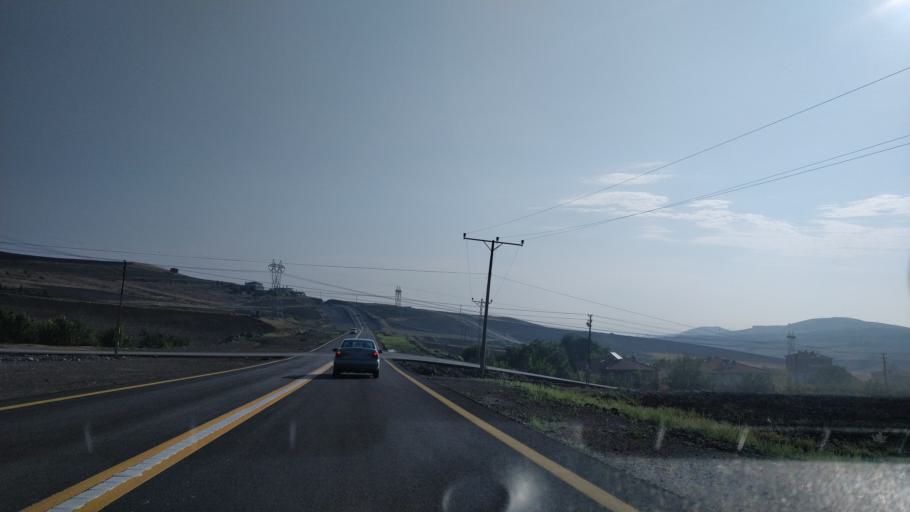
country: TR
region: Ankara
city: Etimesgut
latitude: 39.8631
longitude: 32.5841
